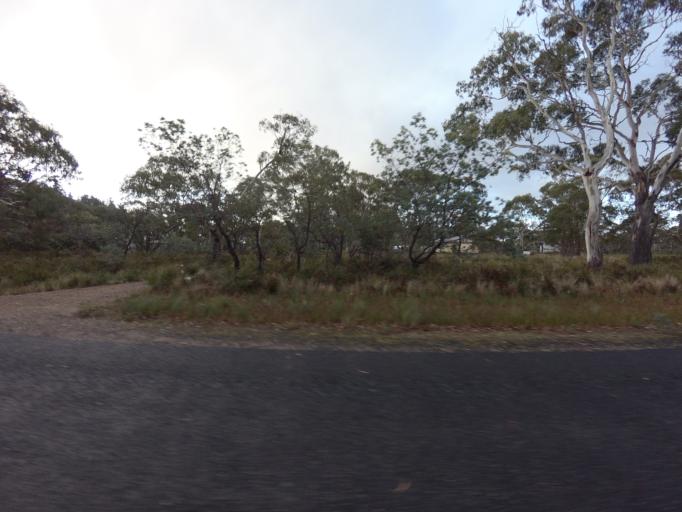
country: AU
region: Tasmania
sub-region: Break O'Day
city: St Helens
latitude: -42.1076
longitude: 148.0723
